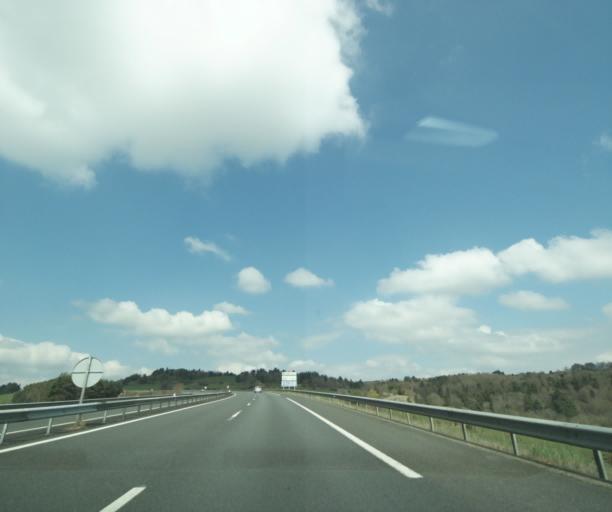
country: FR
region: Auvergne
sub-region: Departement du Cantal
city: Saint-Flour
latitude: 45.0800
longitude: 3.1178
